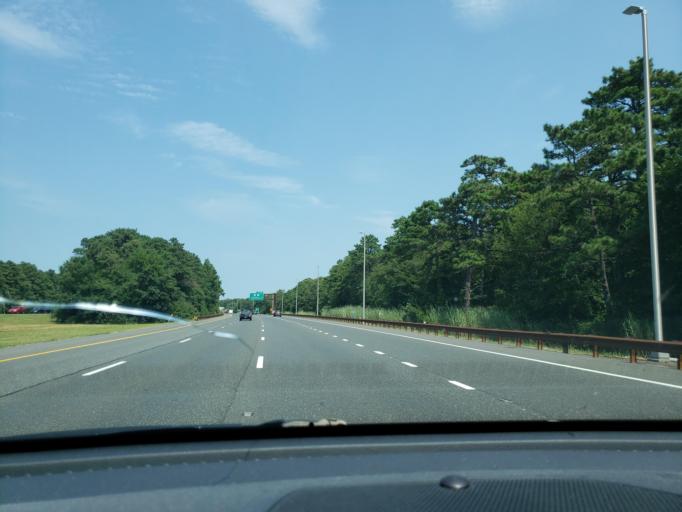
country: US
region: New Jersey
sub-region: Atlantic County
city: Northfield
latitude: 39.3896
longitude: -74.5679
